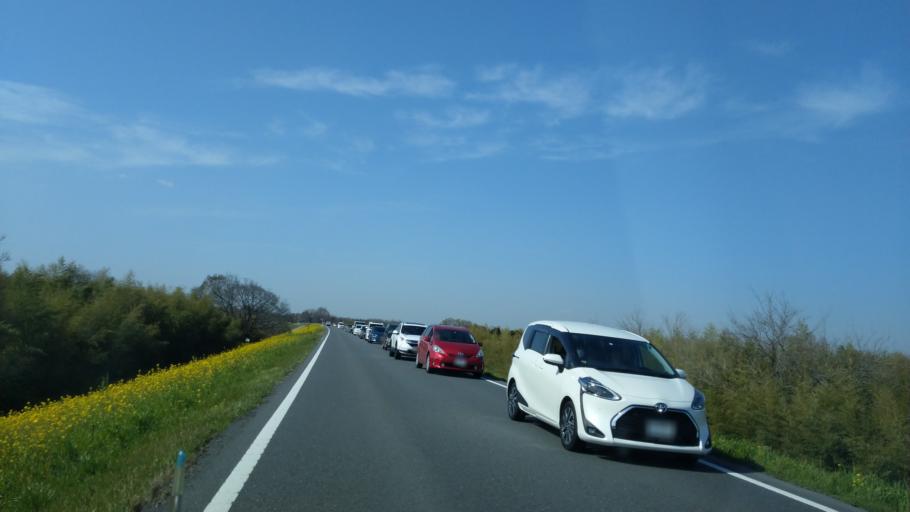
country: JP
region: Saitama
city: Okegawa
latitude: 35.9474
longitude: 139.5345
